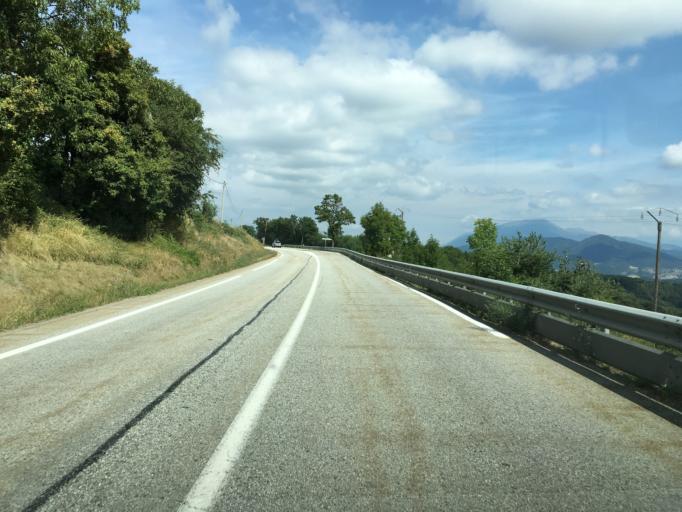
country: FR
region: Rhone-Alpes
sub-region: Departement de l'Isere
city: Mens
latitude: 44.7691
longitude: 5.6626
